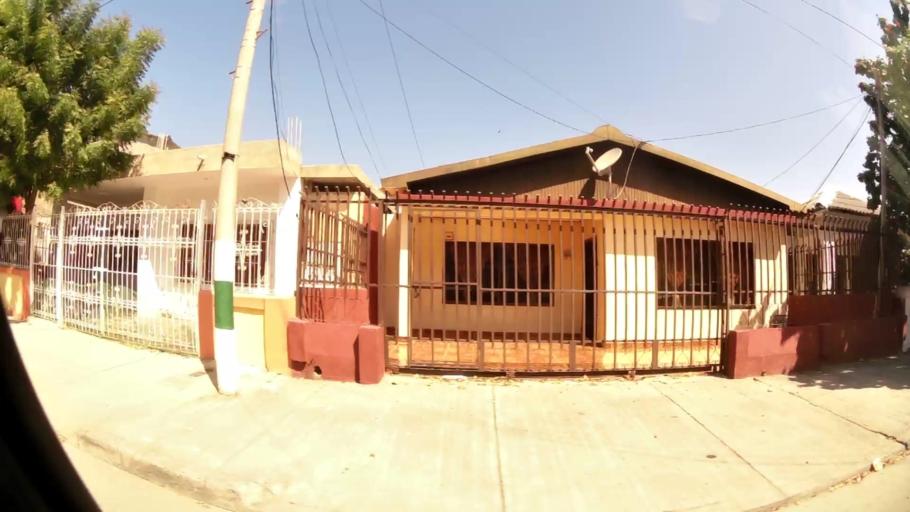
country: CO
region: Bolivar
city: Cartagena
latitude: 10.4414
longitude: -75.5237
